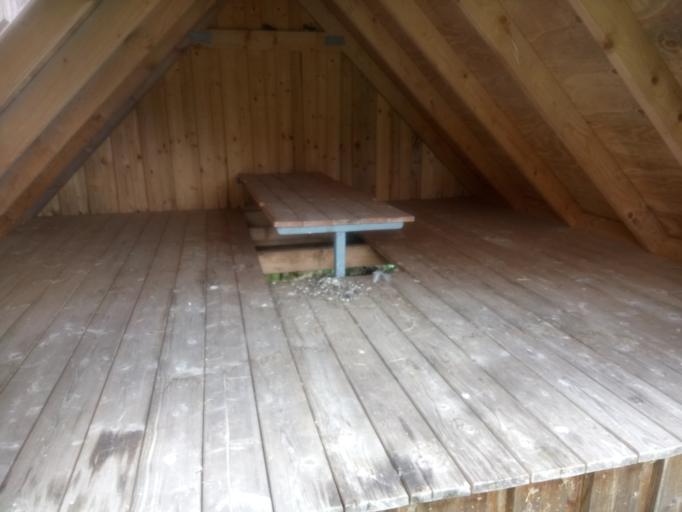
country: DK
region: Central Jutland
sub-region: Herning Kommune
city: Kibaek
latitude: 55.9539
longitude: 8.7235
